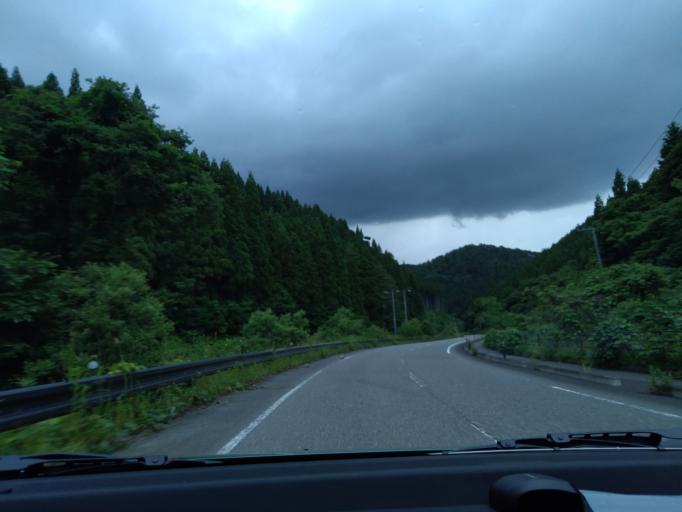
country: JP
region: Miyagi
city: Furukawa
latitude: 38.8164
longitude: 140.9037
